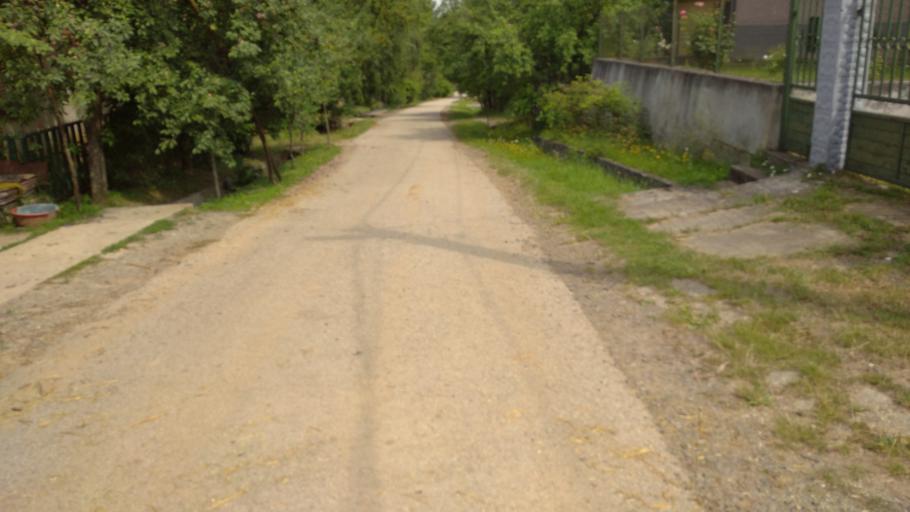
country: SK
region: Nitriansky
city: Sahy
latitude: 47.9897
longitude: 18.8619
